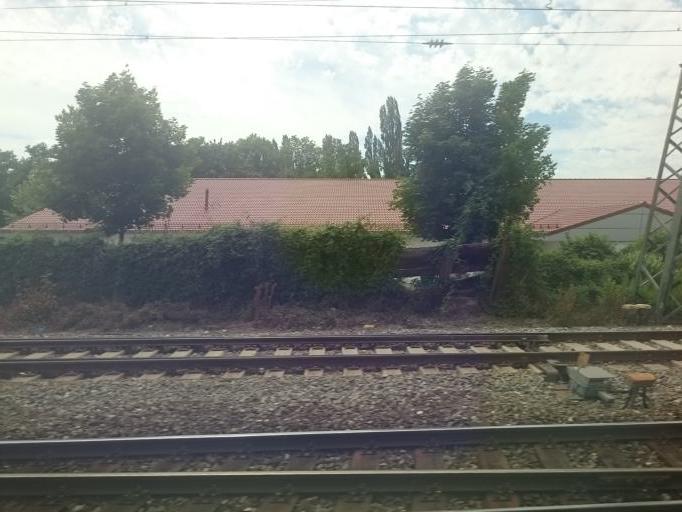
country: DE
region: Bavaria
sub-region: Upper Bavaria
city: Munich
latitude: 48.1204
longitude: 11.5570
